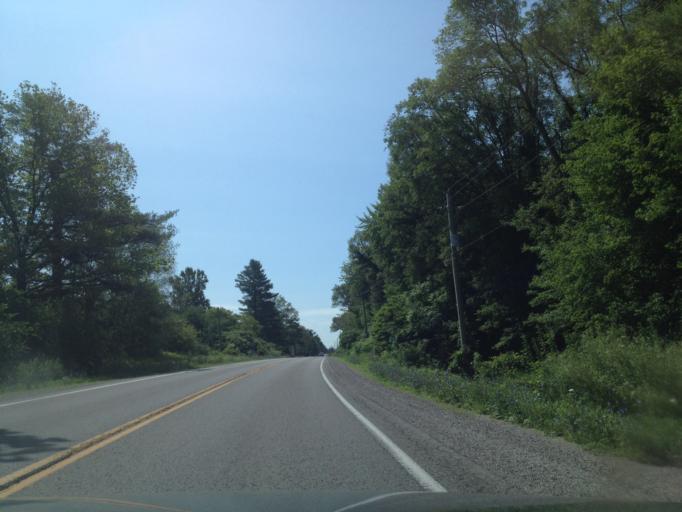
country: CA
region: Ontario
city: Norfolk County
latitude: 42.7748
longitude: -80.3964
